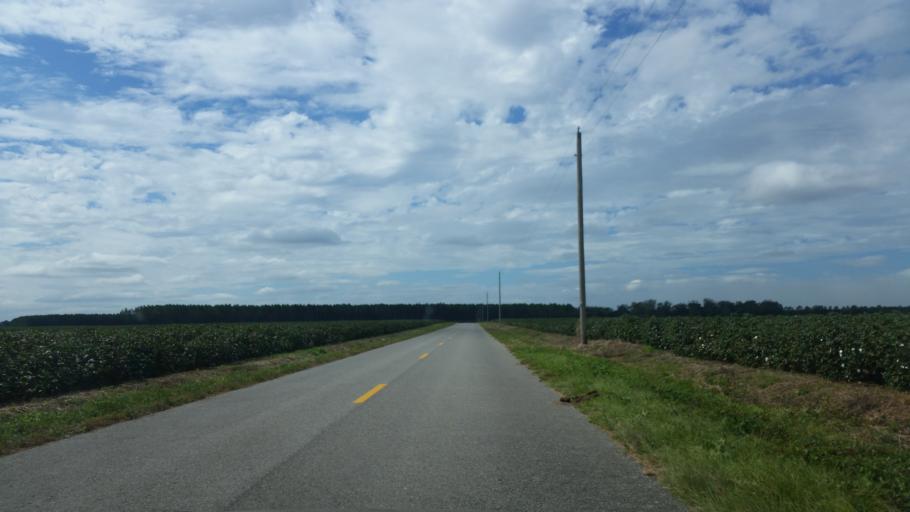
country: US
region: Florida
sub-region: Santa Rosa County
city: Point Baker
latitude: 30.7365
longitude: -87.0235
